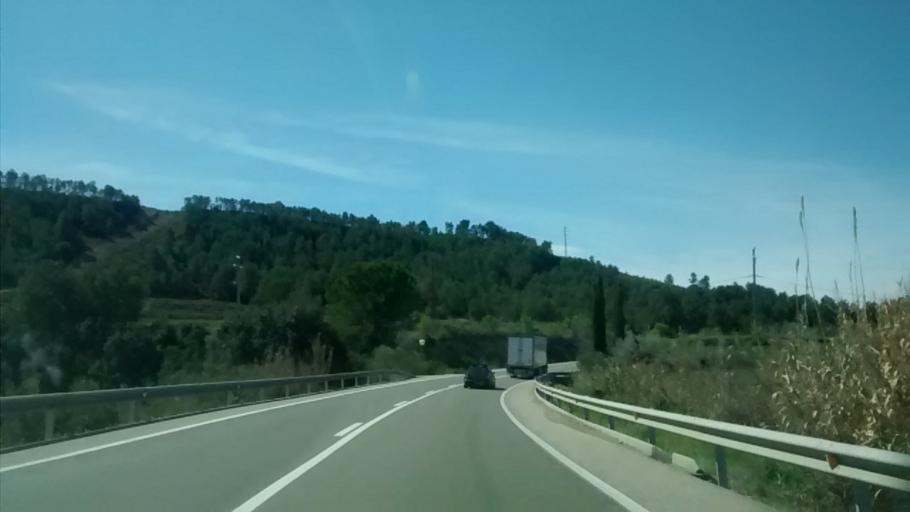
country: ES
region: Catalonia
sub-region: Provincia de Tarragona
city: Ginestar
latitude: 41.0502
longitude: 0.6591
